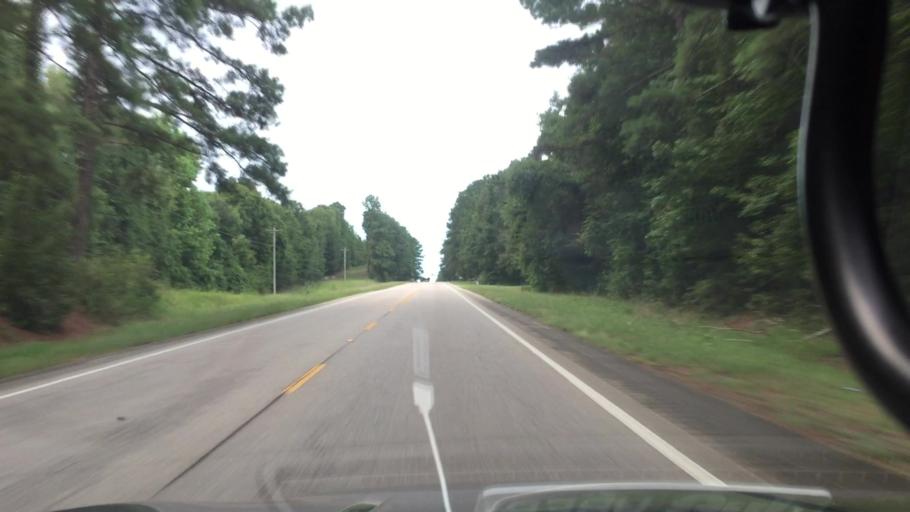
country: US
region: Alabama
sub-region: Pike County
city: Troy
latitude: 31.6629
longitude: -85.9533
